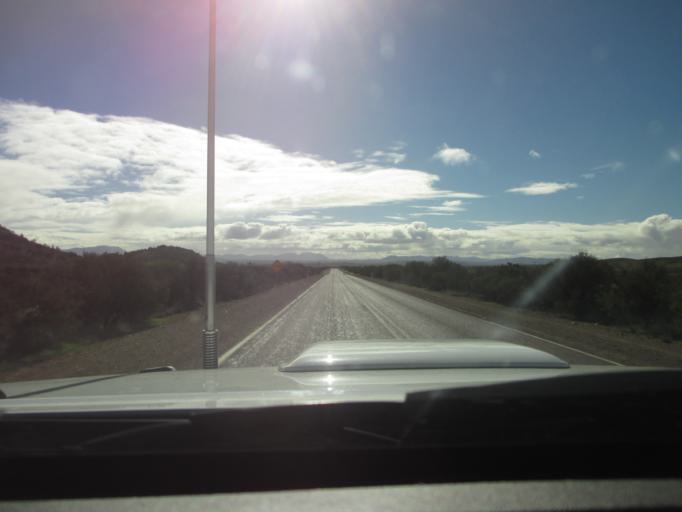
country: AU
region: South Australia
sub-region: Flinders Ranges
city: Quorn
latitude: -31.9236
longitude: 138.4230
